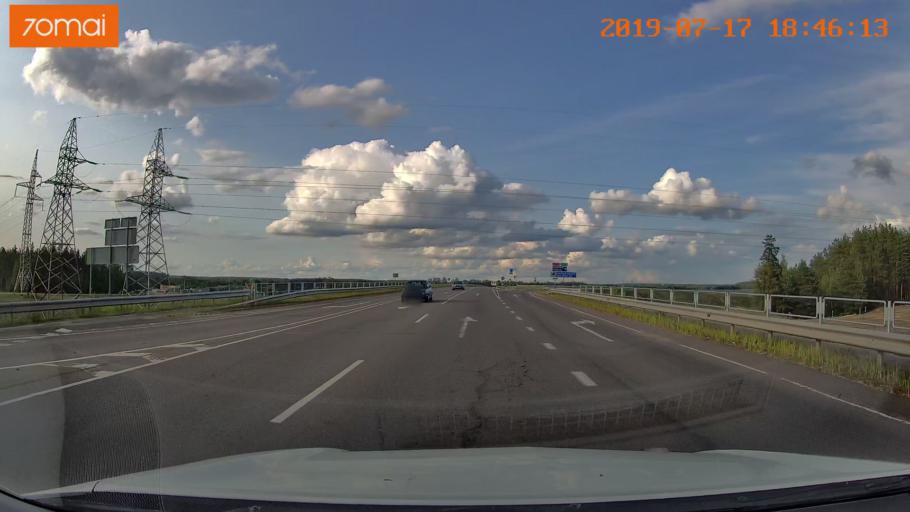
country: BY
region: Mogilev
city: Asipovichy
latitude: 53.3338
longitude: 28.6634
